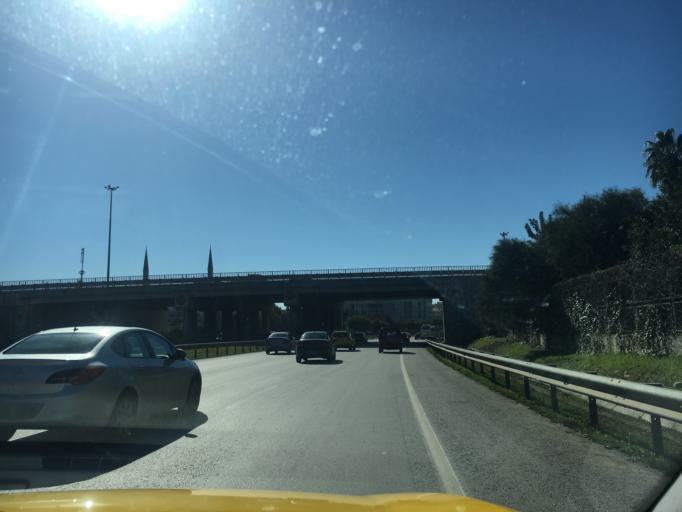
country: TR
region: Antalya
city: Antalya
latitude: 36.9020
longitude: 30.6648
